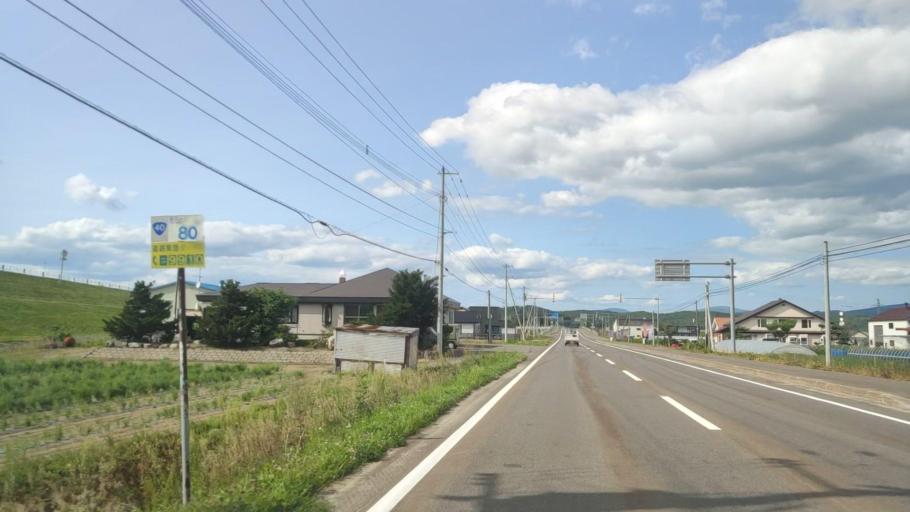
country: JP
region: Hokkaido
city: Nayoro
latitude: 44.3683
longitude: 142.4361
